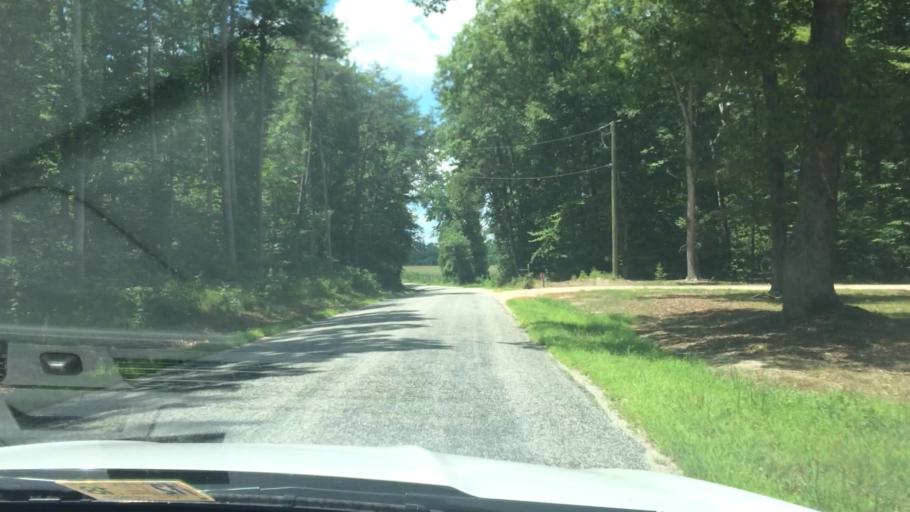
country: US
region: Virginia
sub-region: King William County
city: West Point
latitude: 37.6017
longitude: -76.7879
